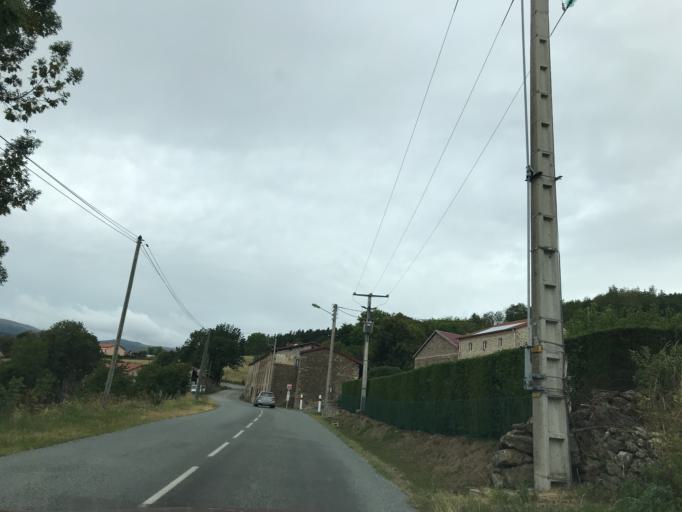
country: FR
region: Rhone-Alpes
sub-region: Departement de la Loire
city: Sail-sous-Couzan
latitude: 45.6924
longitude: 3.8999
